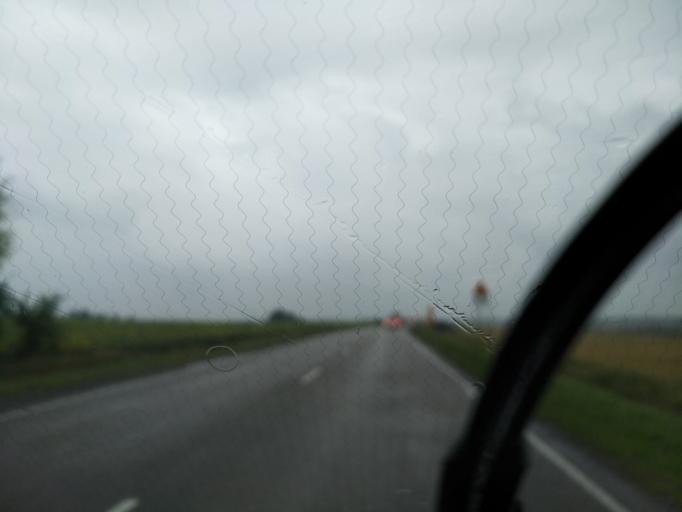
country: RU
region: Voronezj
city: Verkhnyaya Khava
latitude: 51.6784
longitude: 39.7961
